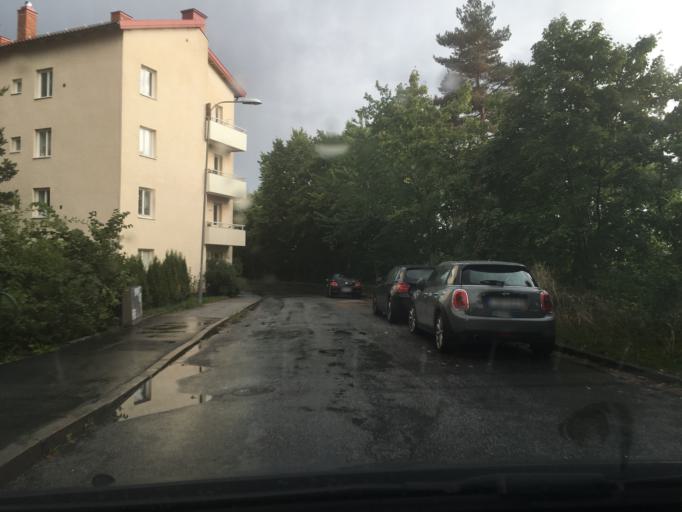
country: SE
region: Stockholm
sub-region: Stockholms Kommun
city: Arsta
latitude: 59.2947
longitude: 18.0735
